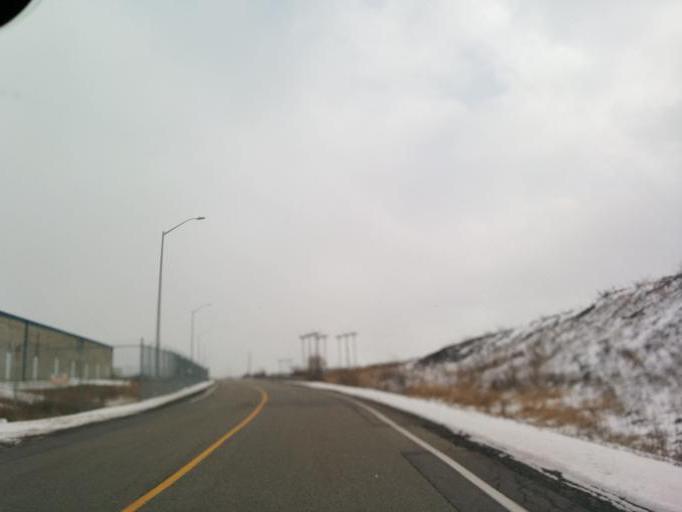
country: CA
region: Ontario
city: Etobicoke
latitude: 43.6695
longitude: -79.6361
